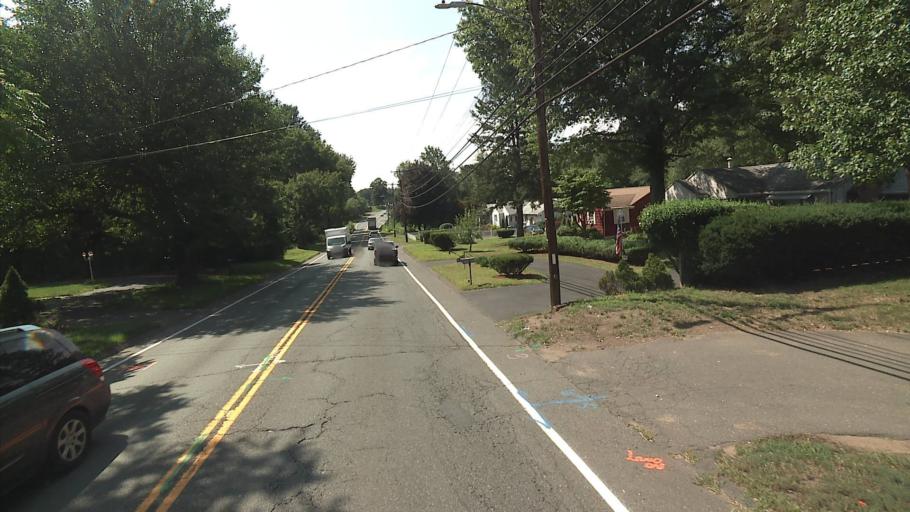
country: US
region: Connecticut
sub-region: Hartford County
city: Windsor
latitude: 41.8554
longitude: -72.6750
